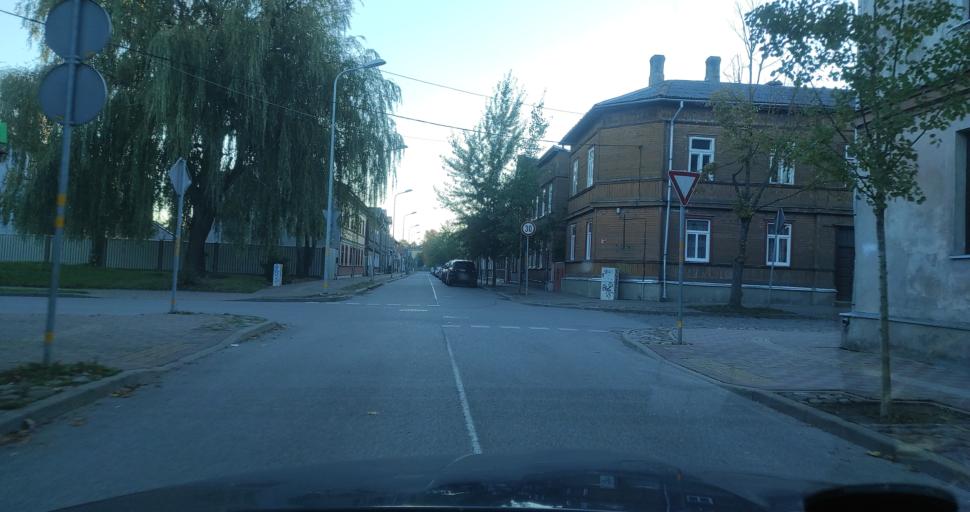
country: LV
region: Liepaja
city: Liepaja
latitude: 56.5034
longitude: 21.0166
